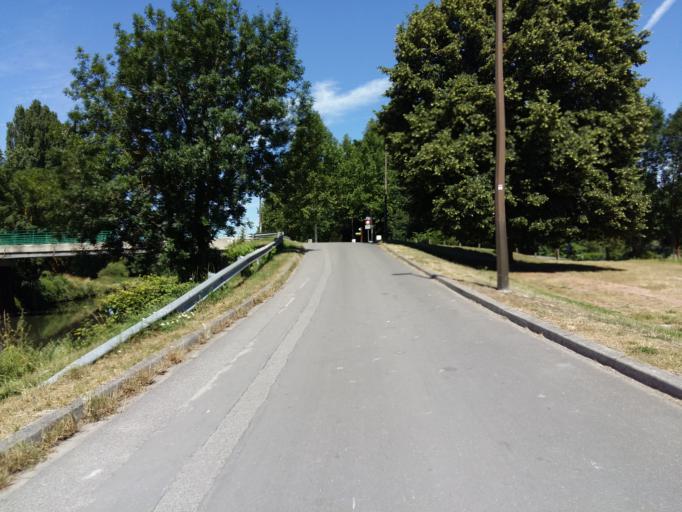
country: FR
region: Picardie
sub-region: Departement de la Somme
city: Amiens
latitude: 49.9091
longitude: 2.2815
